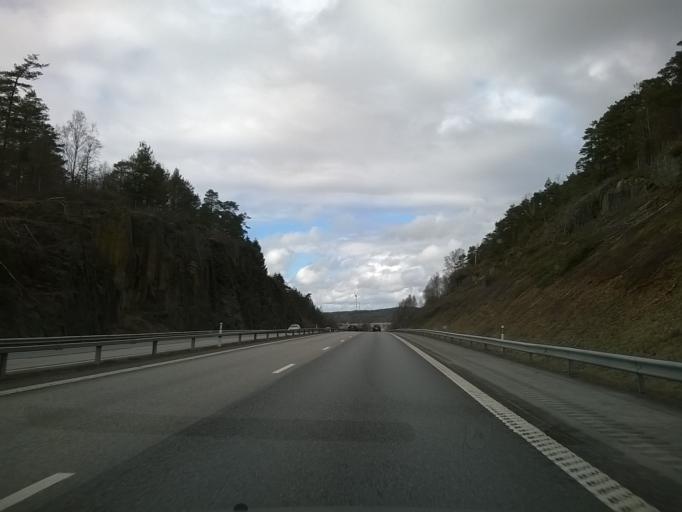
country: SE
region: Halland
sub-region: Kungsbacka Kommun
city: Frillesas
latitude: 57.3113
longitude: 12.2124
